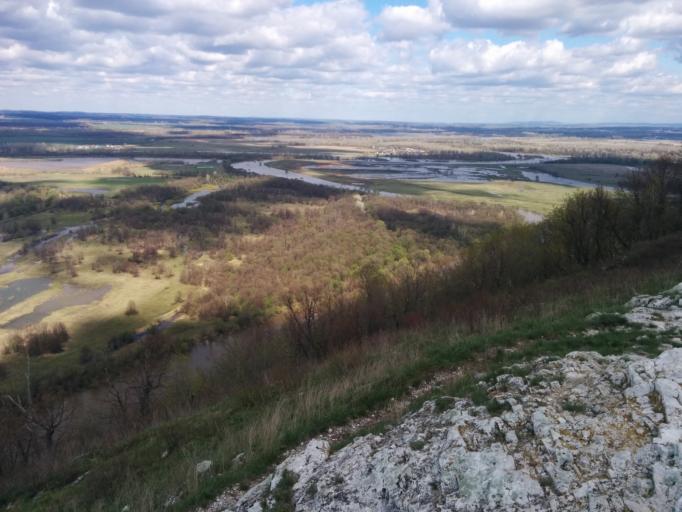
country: RU
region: Bashkortostan
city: Sterlitamak
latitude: 53.7413
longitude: 56.0938
